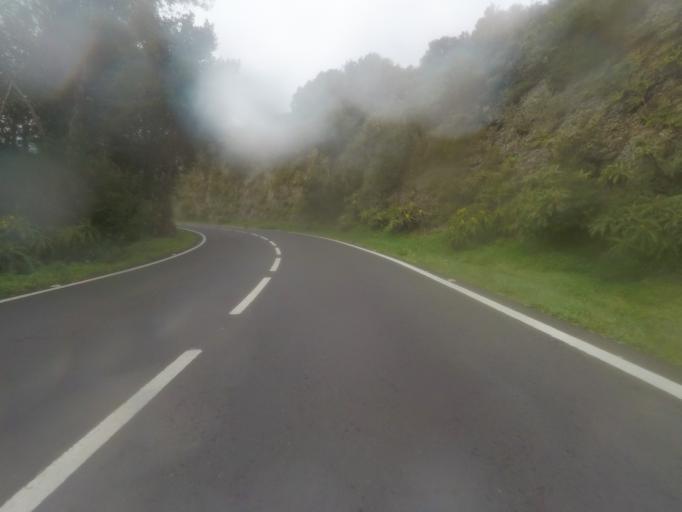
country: ES
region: Canary Islands
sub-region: Provincia de Santa Cruz de Tenerife
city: Vallehermosa
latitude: 28.1263
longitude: -17.2614
